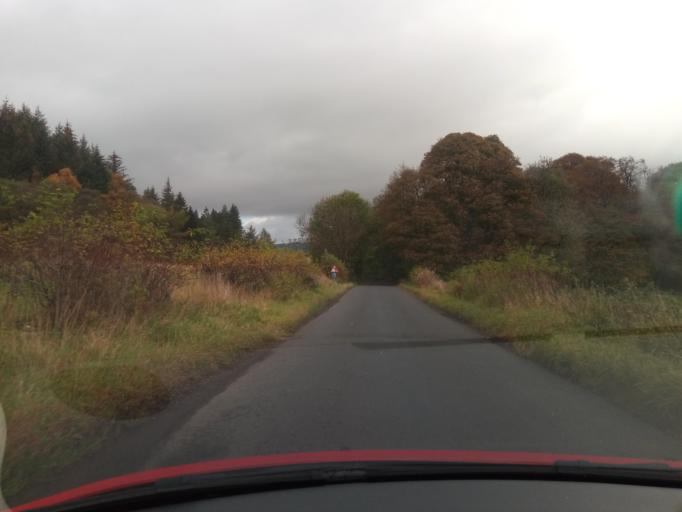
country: GB
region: Scotland
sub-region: The Scottish Borders
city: Innerleithen
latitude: 55.6194
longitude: -3.0909
